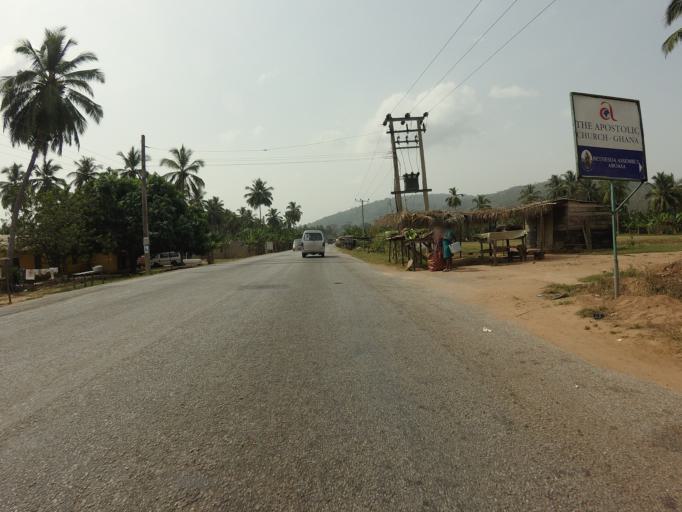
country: GH
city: Akropong
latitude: 6.2960
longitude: 0.1340
